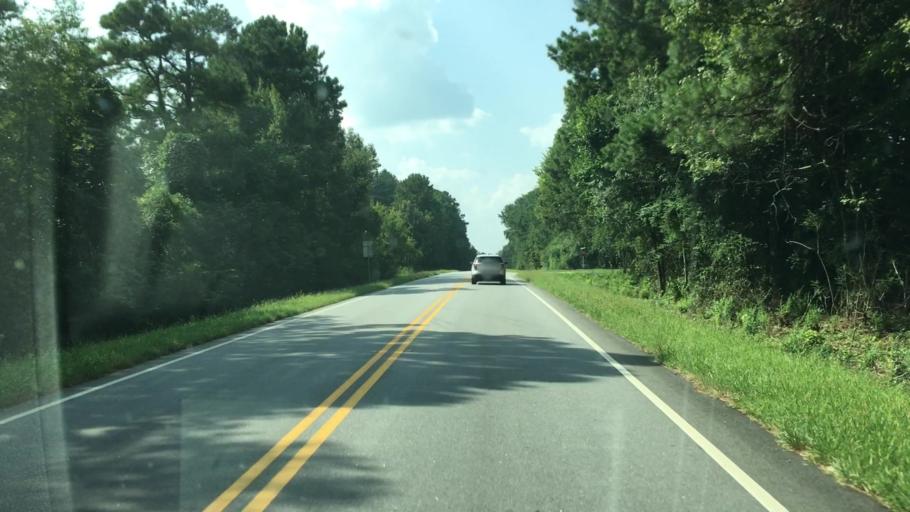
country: US
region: Georgia
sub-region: Jasper County
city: Monticello
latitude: 33.3242
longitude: -83.7018
